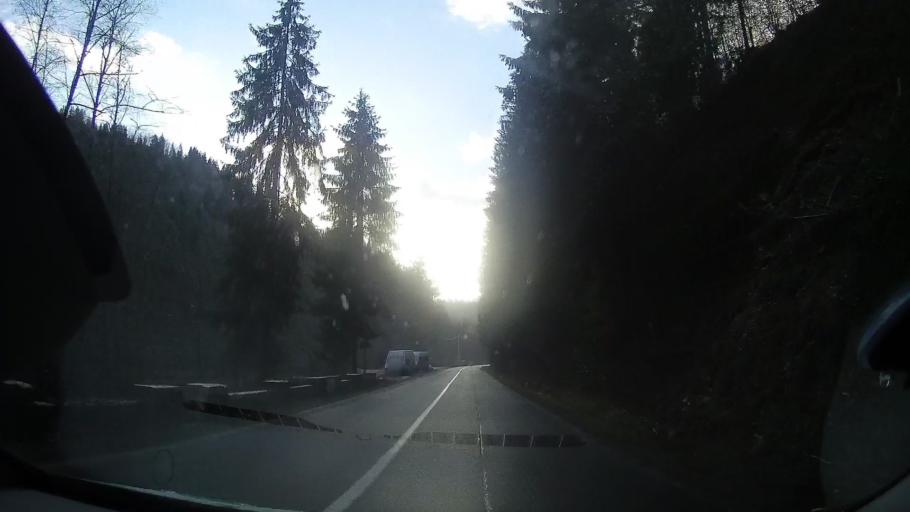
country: RO
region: Alba
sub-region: Comuna Albac
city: Albac
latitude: 46.4292
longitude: 22.9641
